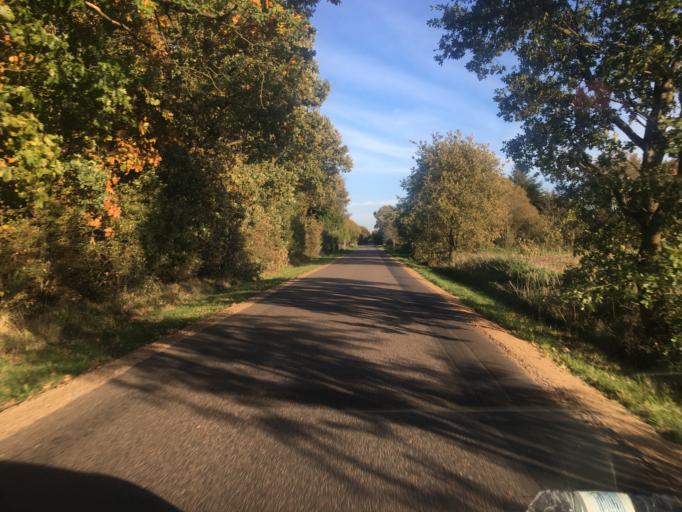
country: DE
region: Schleswig-Holstein
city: Ellhoft
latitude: 54.9149
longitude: 8.9792
